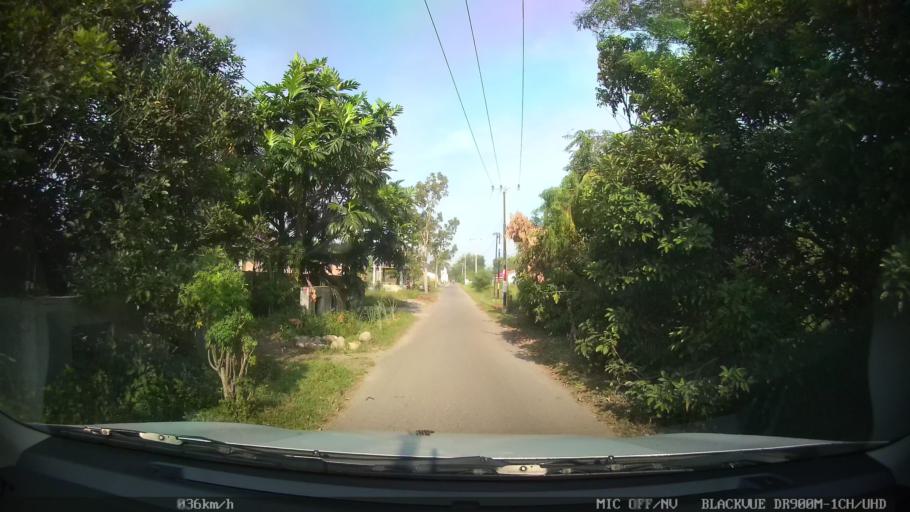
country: ID
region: North Sumatra
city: Binjai
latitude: 3.6210
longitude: 98.5218
